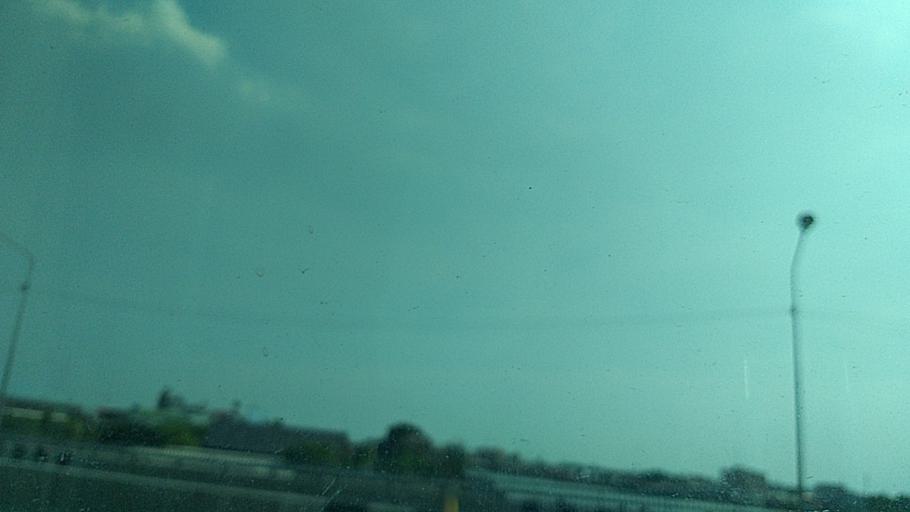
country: TH
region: Pathum Thani
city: Pathum Thani
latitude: 14.0256
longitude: 100.5393
